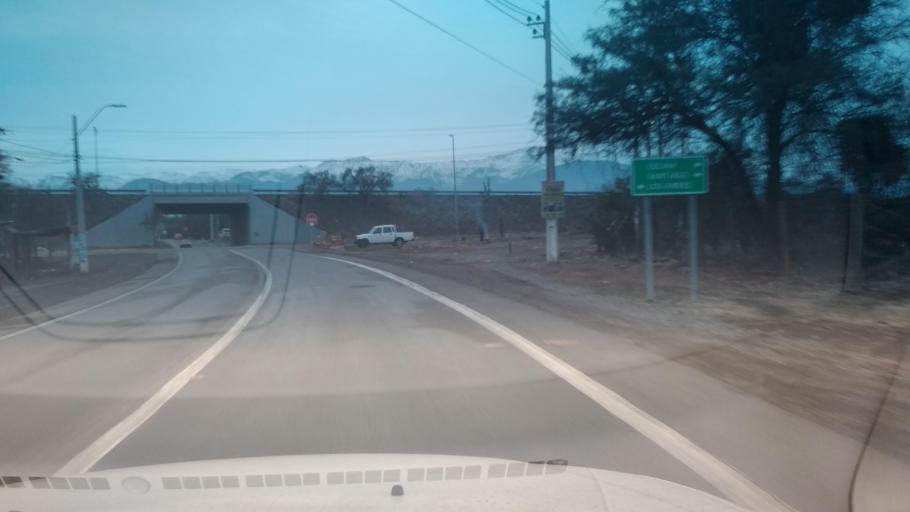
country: CL
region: Santiago Metropolitan
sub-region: Provincia de Chacabuco
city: Chicureo Abajo
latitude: -33.0951
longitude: -70.6940
